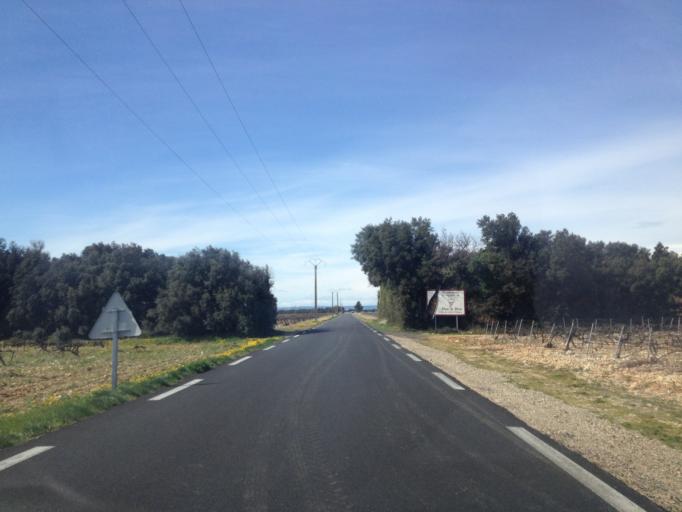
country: FR
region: Provence-Alpes-Cote d'Azur
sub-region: Departement du Vaucluse
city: Violes
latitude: 44.1901
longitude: 4.9650
